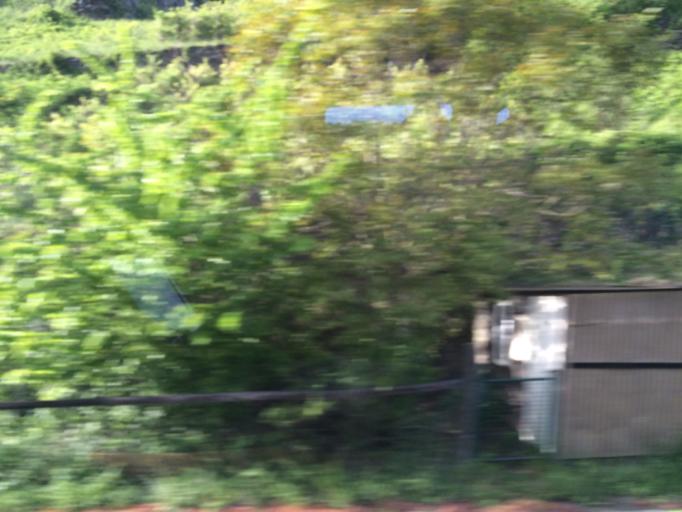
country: DE
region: Rheinland-Pfalz
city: Prath
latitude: 50.1718
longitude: 7.6827
